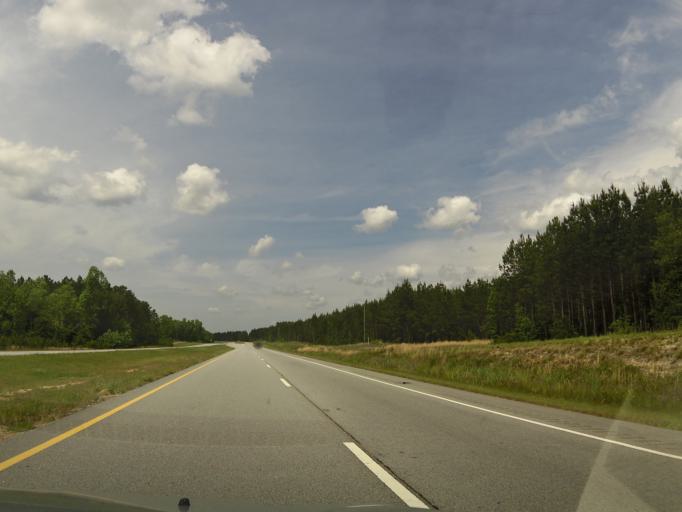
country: US
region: Georgia
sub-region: Jefferson County
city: Wadley
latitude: 32.7626
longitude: -82.3854
